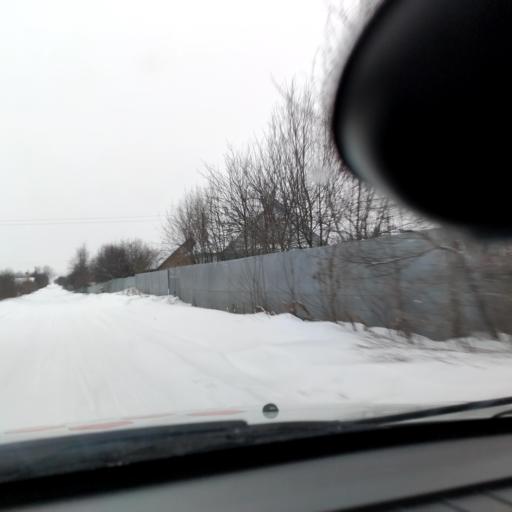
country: RU
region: Bashkortostan
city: Avdon
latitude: 54.5709
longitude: 55.7386
